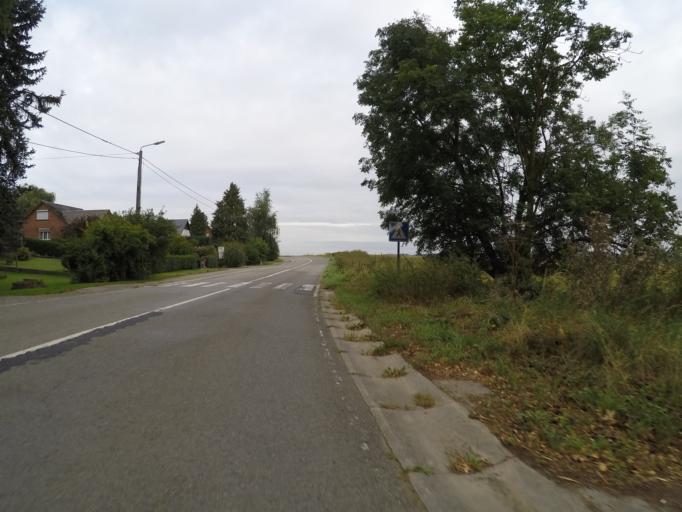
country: BE
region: Wallonia
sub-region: Province de Namur
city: Ciney
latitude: 50.3121
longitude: 5.0541
